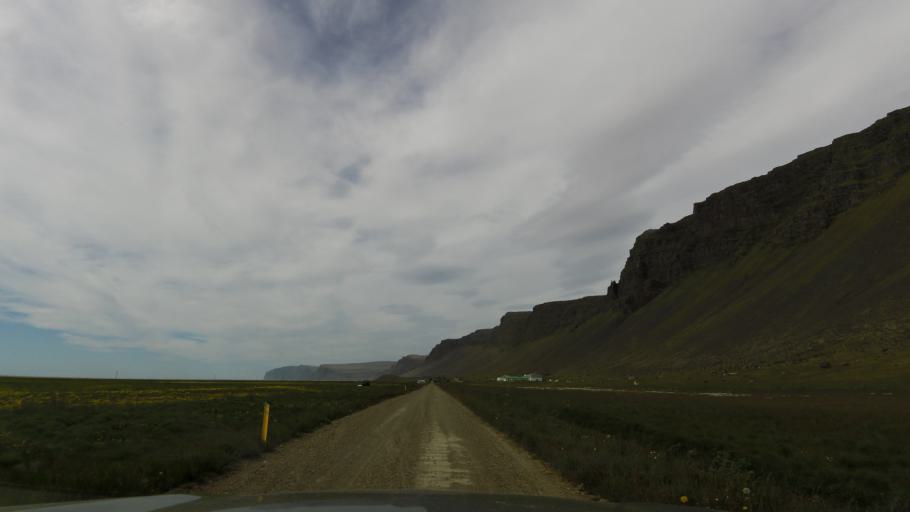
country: IS
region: West
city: Olafsvik
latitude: 65.4916
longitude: -24.0836
